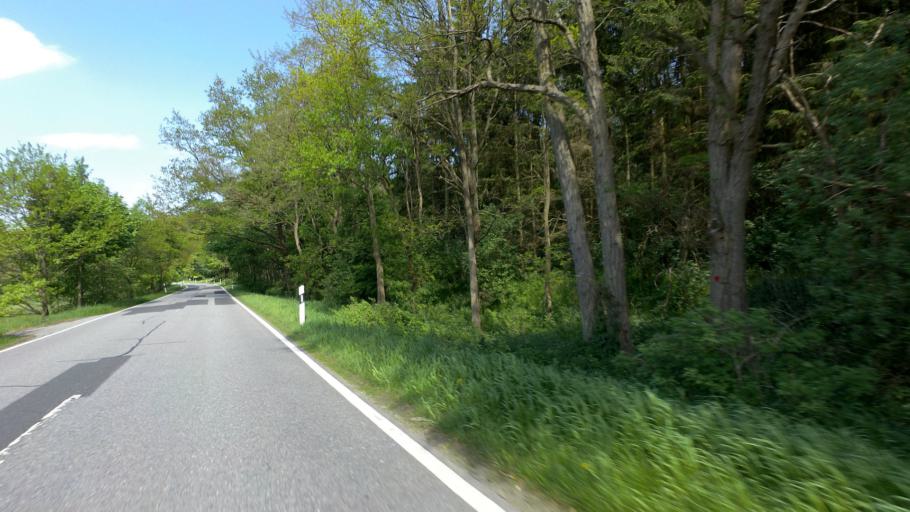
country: DE
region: Mecklenburg-Vorpommern
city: Mollenhagen
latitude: 53.5541
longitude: 12.9217
